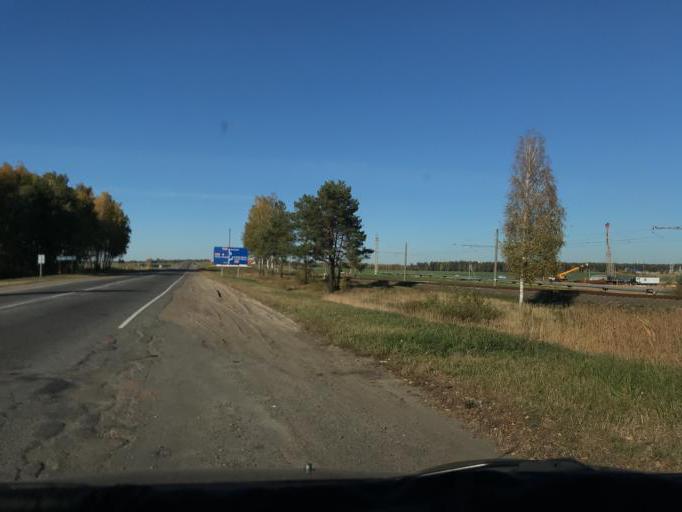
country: BY
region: Gomel
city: Mazyr
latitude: 51.9997
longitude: 29.2574
